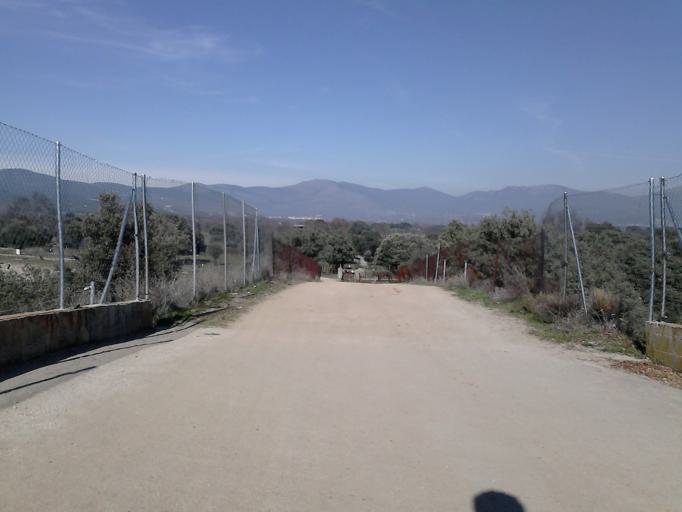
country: ES
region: Madrid
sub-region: Provincia de Madrid
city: Navalquejigo
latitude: 40.6108
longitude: -4.0734
